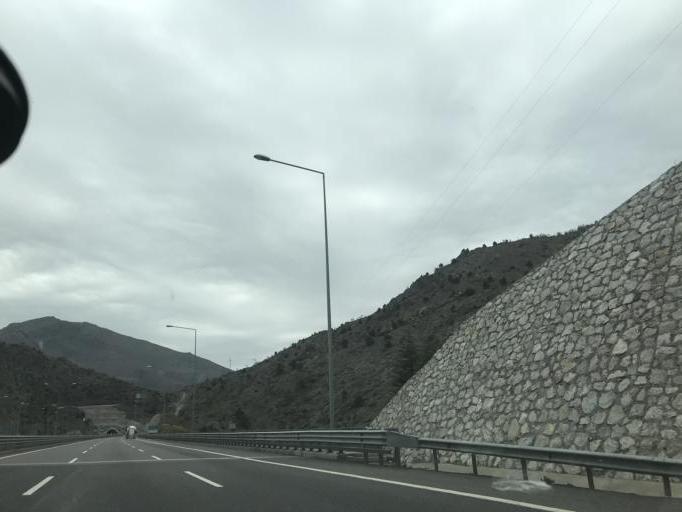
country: TR
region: Nigde
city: Ciftehan
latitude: 37.5531
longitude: 34.7747
